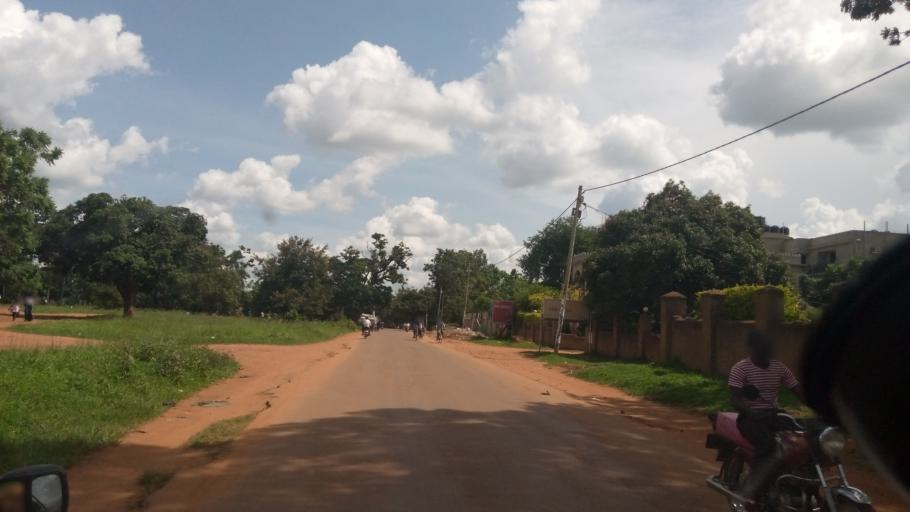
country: UG
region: Northern Region
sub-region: Lira District
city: Lira
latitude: 2.2510
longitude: 32.8997
